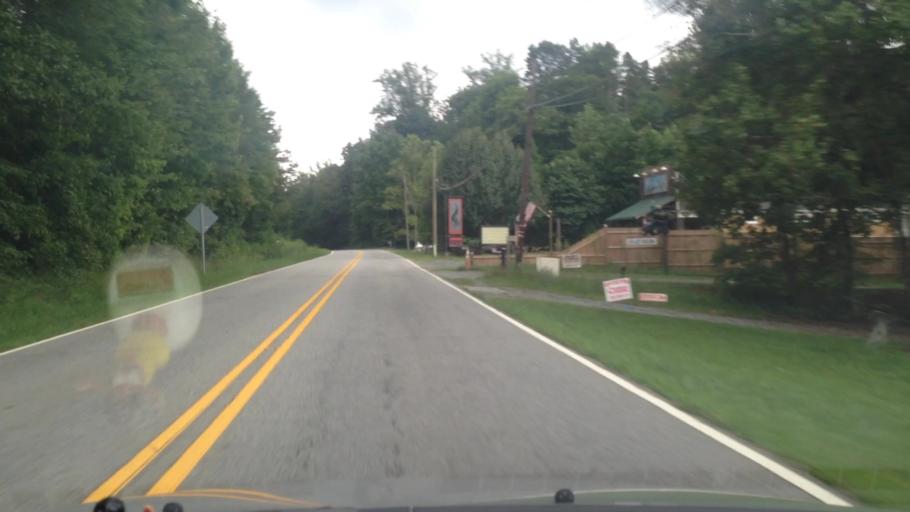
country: US
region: North Carolina
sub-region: Forsyth County
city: Walkertown
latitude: 36.2008
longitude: -80.1664
